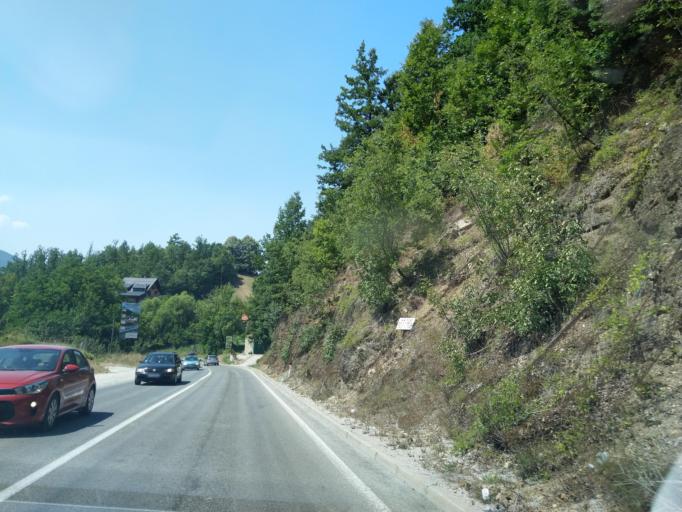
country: RS
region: Central Serbia
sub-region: Zlatiborski Okrug
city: Nova Varos
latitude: 43.4615
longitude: 19.7766
